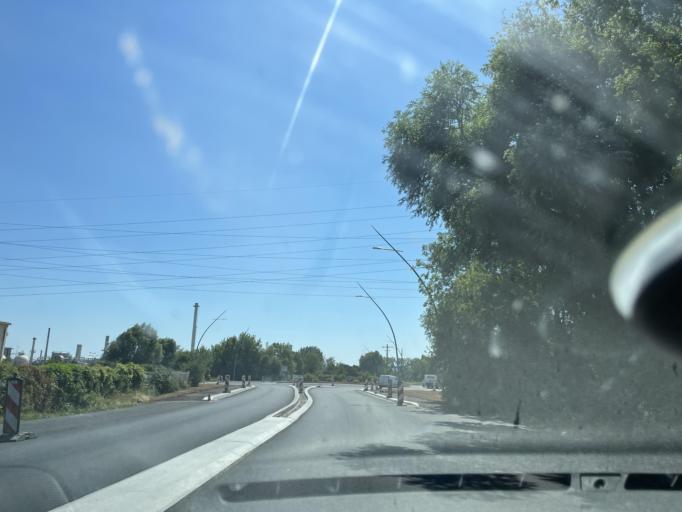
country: FR
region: Haute-Normandie
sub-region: Departement de l'Eure
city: Quillebeuf-sur-Seine
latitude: 49.4941
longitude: 0.5350
